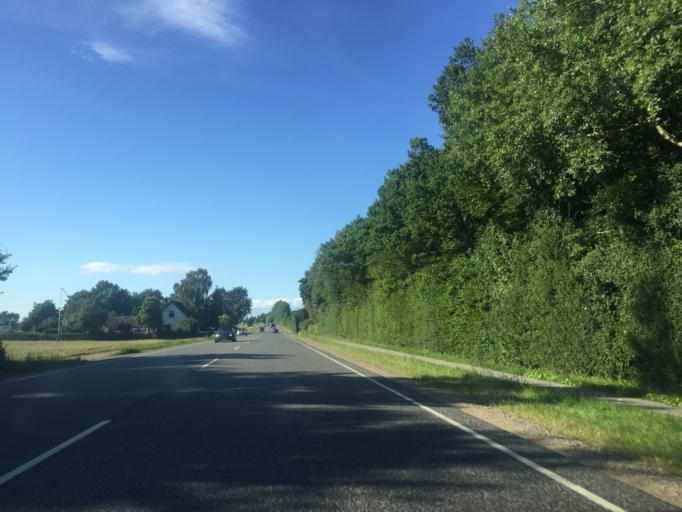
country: DK
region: Zealand
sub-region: Guldborgsund Kommune
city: Nykobing Falster
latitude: 54.8246
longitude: 11.8671
